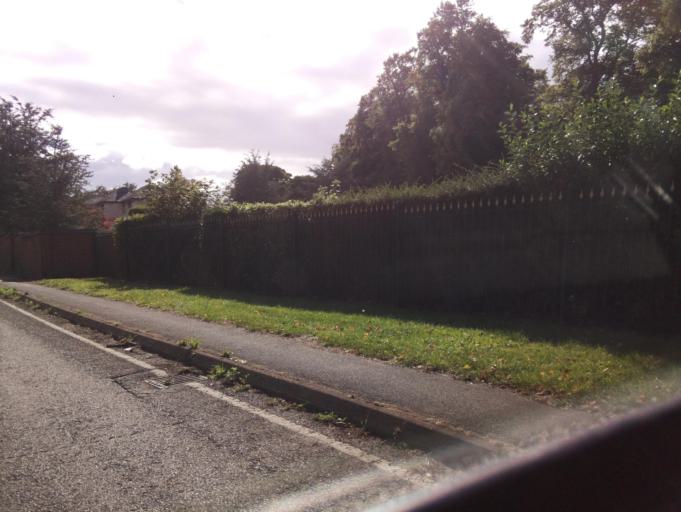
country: GB
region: England
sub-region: Leicestershire
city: Ashby de la Zouch
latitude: 52.7374
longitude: -1.4824
